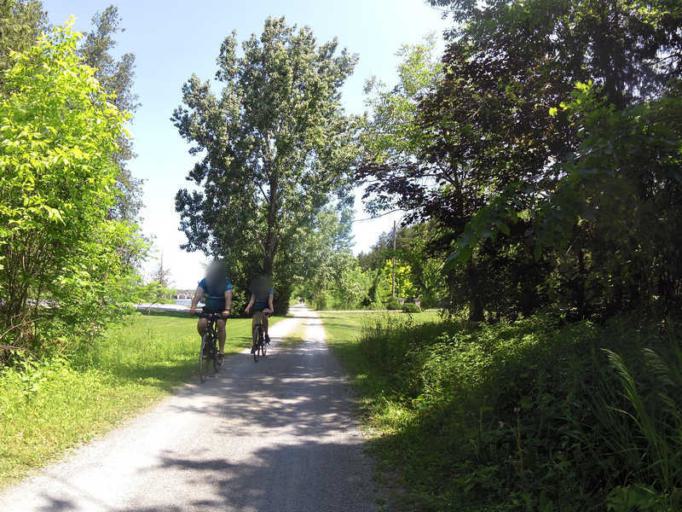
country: CA
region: Ontario
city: Peterborough
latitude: 44.3966
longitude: -78.2638
